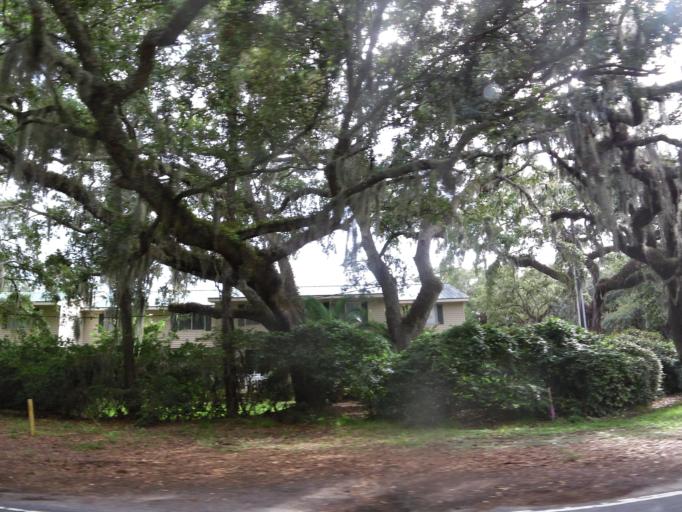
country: US
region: Georgia
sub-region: Glynn County
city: Saint Simons Island
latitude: 31.1482
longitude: -81.3811
